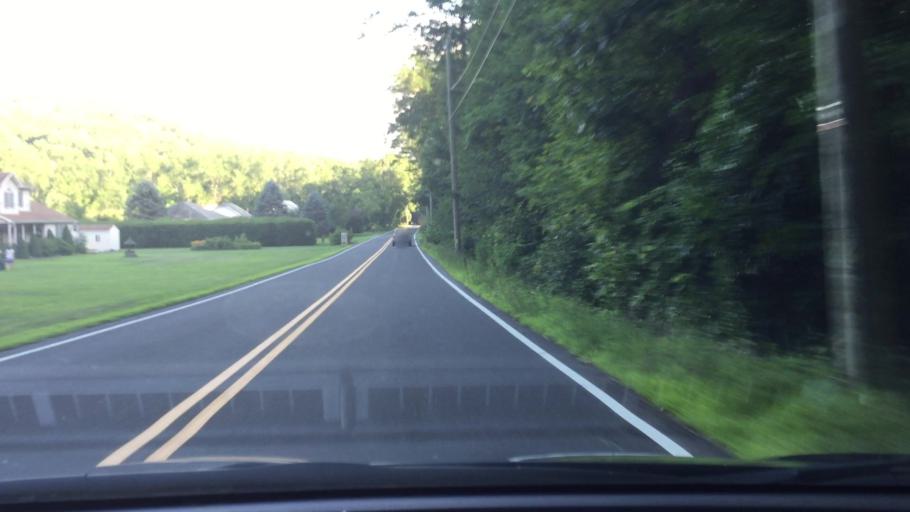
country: US
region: Massachusetts
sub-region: Hampshire County
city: Westhampton
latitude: 42.2252
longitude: -72.8557
